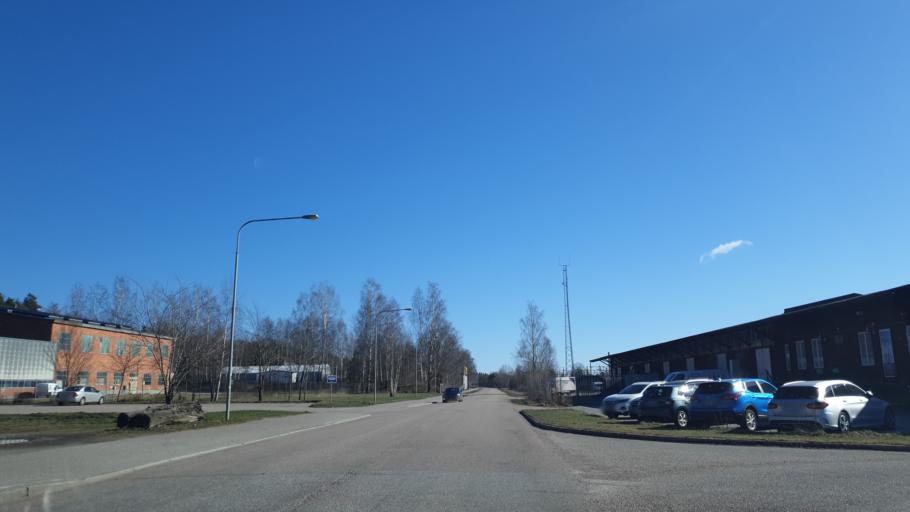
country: SE
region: Vaestmanland
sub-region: Kopings Kommun
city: Koping
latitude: 59.5068
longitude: 16.0062
